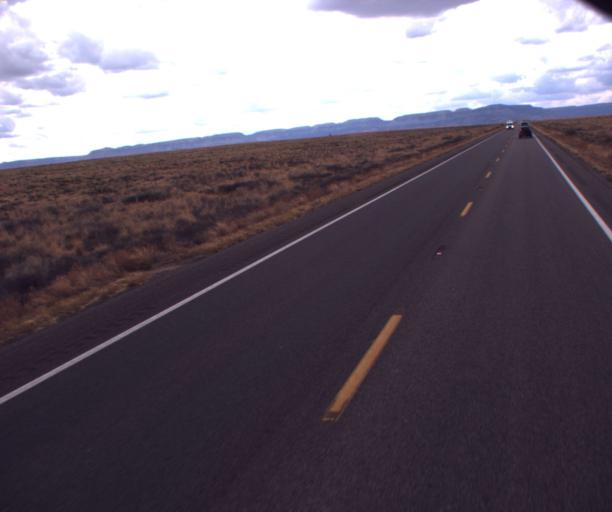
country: US
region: Arizona
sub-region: Navajo County
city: Kayenta
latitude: 36.7371
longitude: -110.0889
